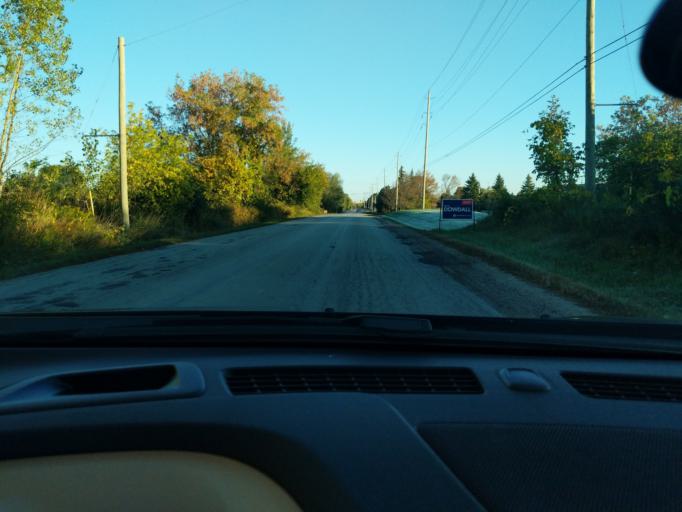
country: CA
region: Ontario
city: Collingwood
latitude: 44.4967
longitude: -80.2500
